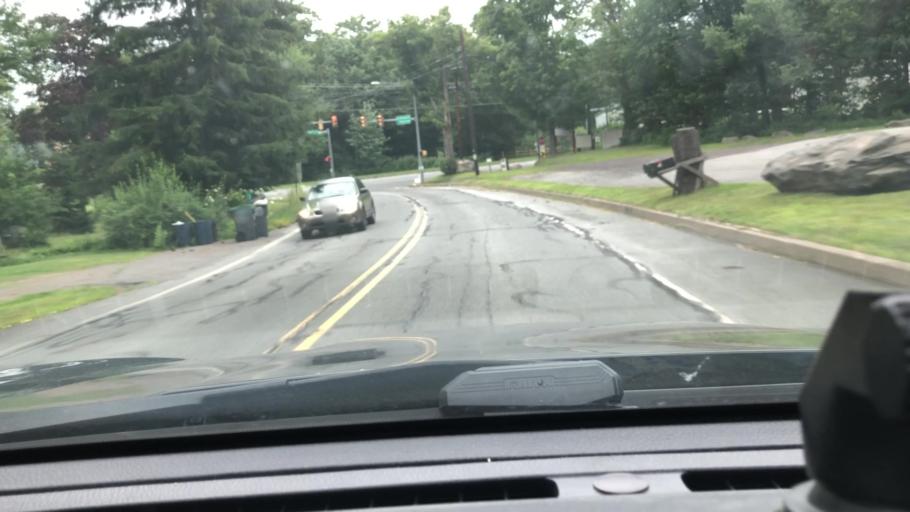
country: US
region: Pennsylvania
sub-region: Lackawanna County
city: Moscow
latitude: 41.2525
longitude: -75.5028
